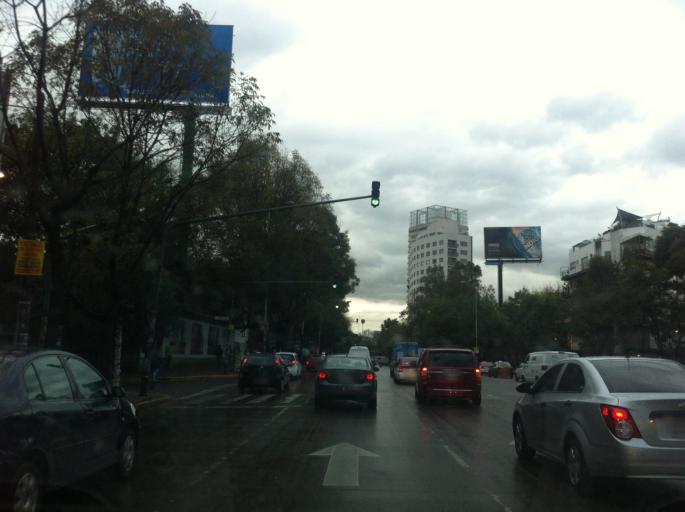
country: MX
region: Mexico City
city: Polanco
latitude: 19.4077
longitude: -99.1790
